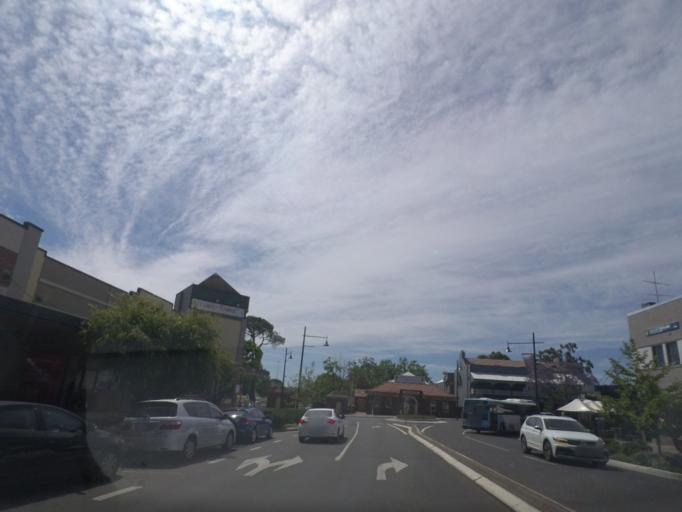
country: AU
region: New South Wales
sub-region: Camden
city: Elderslie
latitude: -34.0560
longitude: 150.6937
